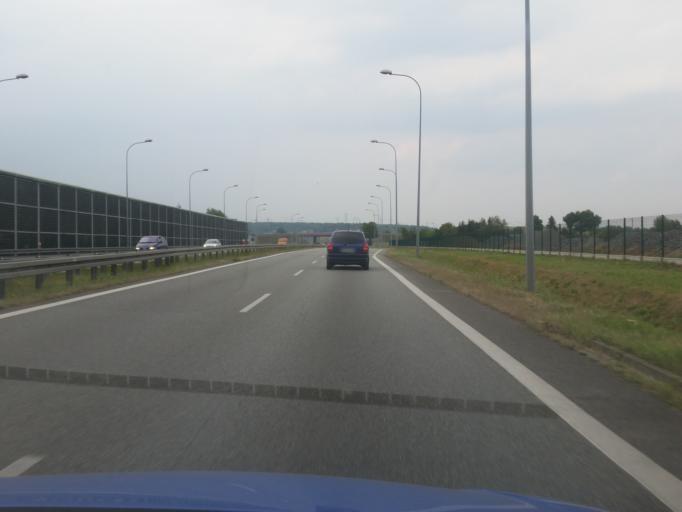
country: PL
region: Silesian Voivodeship
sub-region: Powiat bedzinski
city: Siewierz
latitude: 50.4155
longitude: 19.2070
